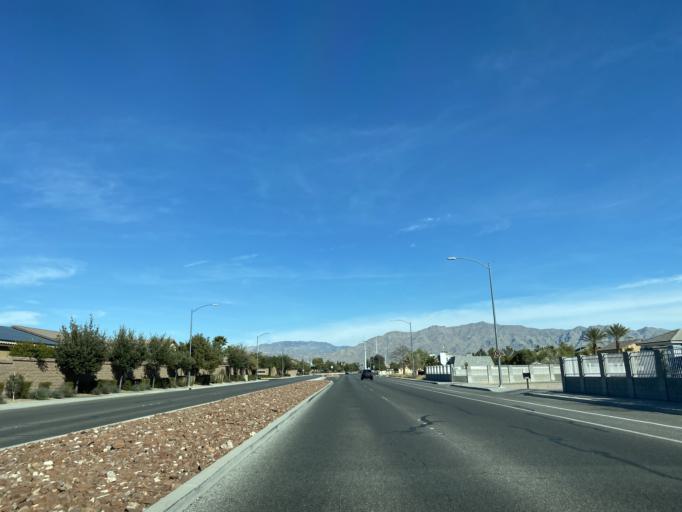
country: US
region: Nevada
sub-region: Clark County
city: Las Vegas
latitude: 36.2653
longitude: -115.2254
